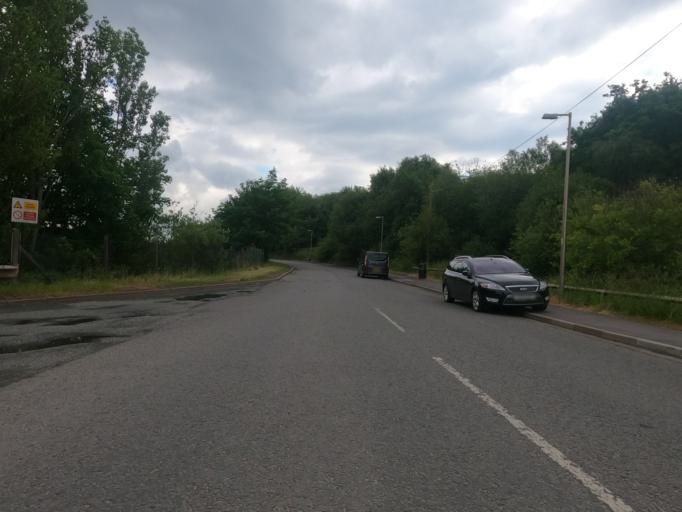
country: GB
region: England
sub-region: Cheshire West and Chester
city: Winsford
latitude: 53.2065
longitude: -2.5215
